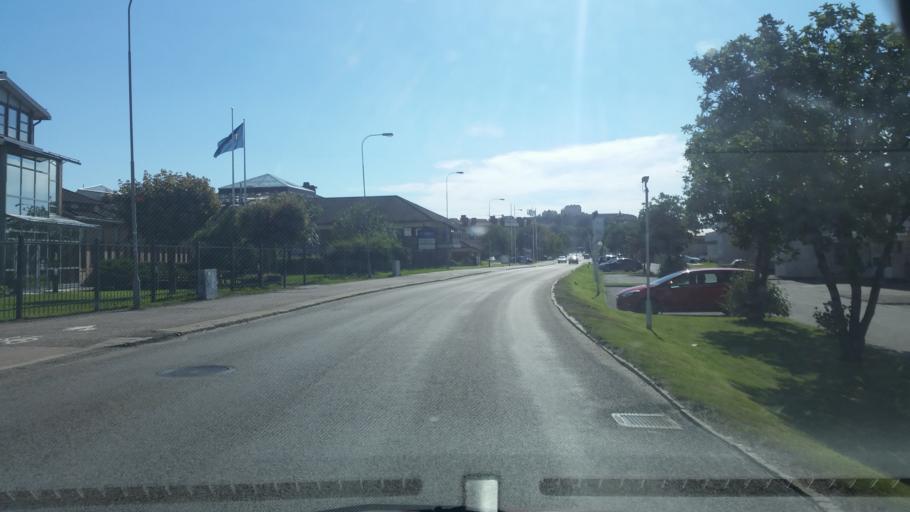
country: SE
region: Vaestra Goetaland
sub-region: Goteborg
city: Eriksbo
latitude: 57.7251
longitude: 12.0353
